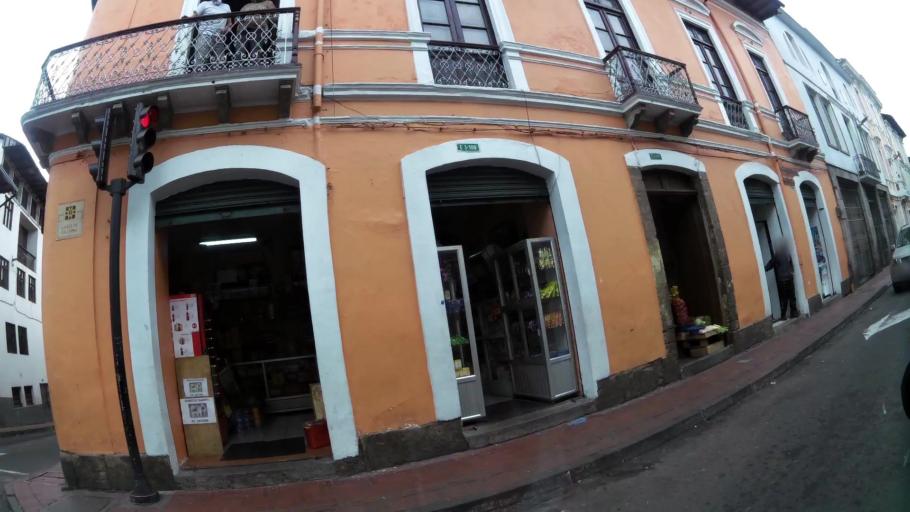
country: EC
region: Pichincha
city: Quito
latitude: -0.2250
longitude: -78.5120
